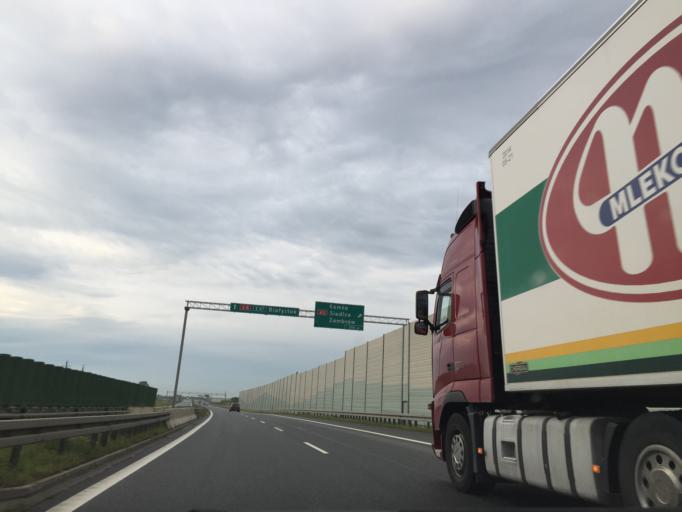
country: PL
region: Podlasie
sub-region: Powiat zambrowski
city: Zambrow
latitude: 52.9678
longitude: 22.2051
